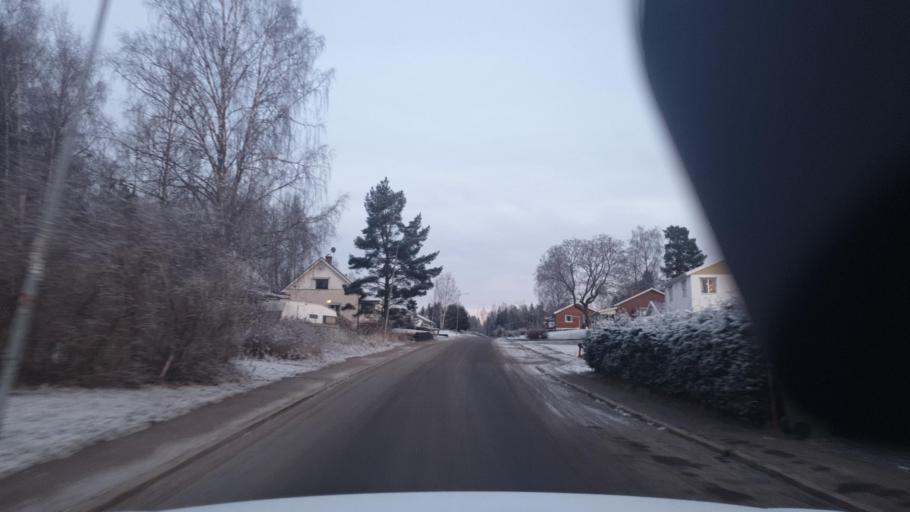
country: SE
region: Vaermland
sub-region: Eda Kommun
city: Amotfors
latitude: 59.7708
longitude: 12.3693
